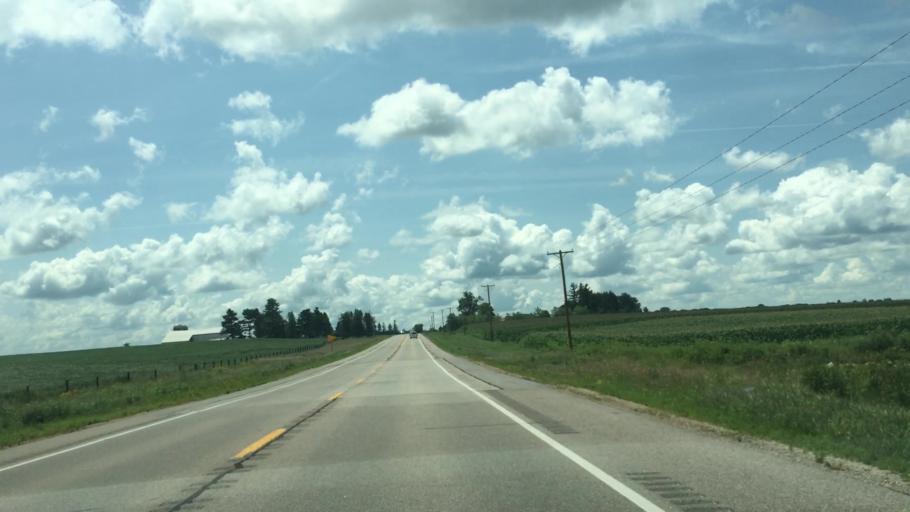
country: US
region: Iowa
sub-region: Johnson County
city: Solon
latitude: 41.8265
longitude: -91.4975
